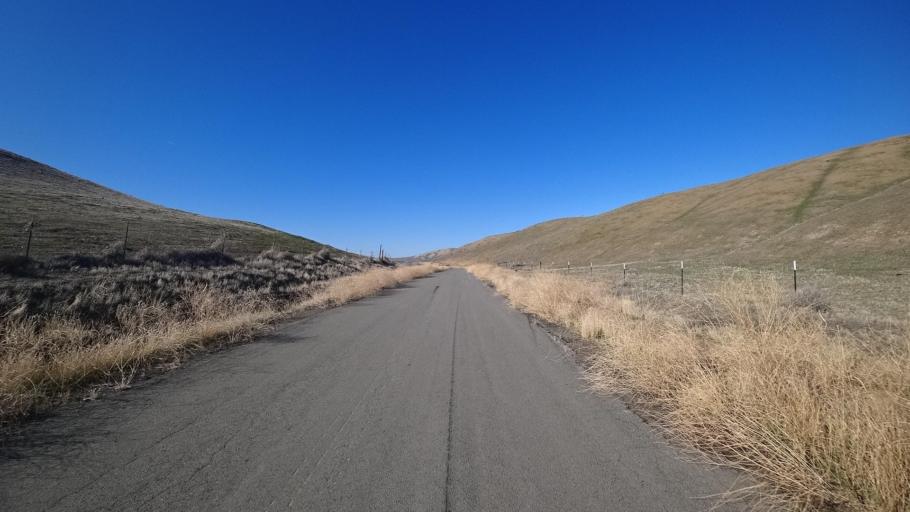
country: US
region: California
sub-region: Kern County
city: Maricopa
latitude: 34.9803
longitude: -119.4671
